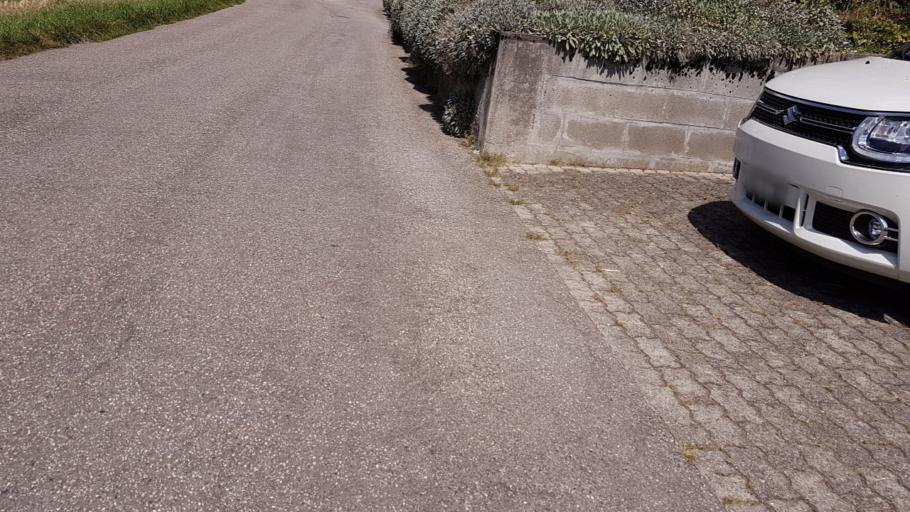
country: CH
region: Lucerne
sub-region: Entlebuch District
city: Oberdiessbach
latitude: 46.8454
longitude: 7.6223
